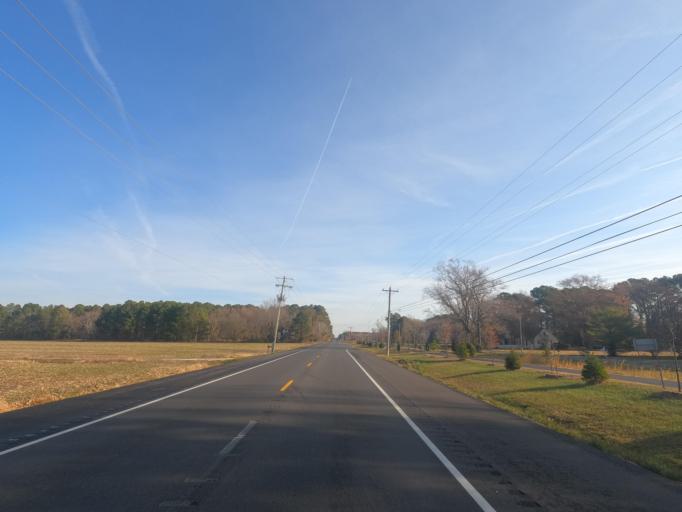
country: US
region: Maryland
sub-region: Somerset County
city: Crisfield
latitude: 38.0352
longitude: -75.7777
